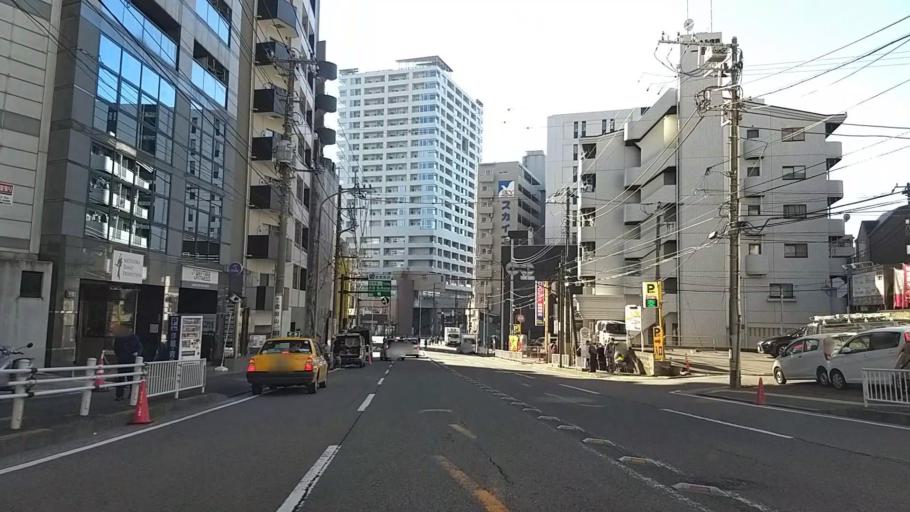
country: JP
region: Kanagawa
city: Yokohama
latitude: 35.4472
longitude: 139.6274
